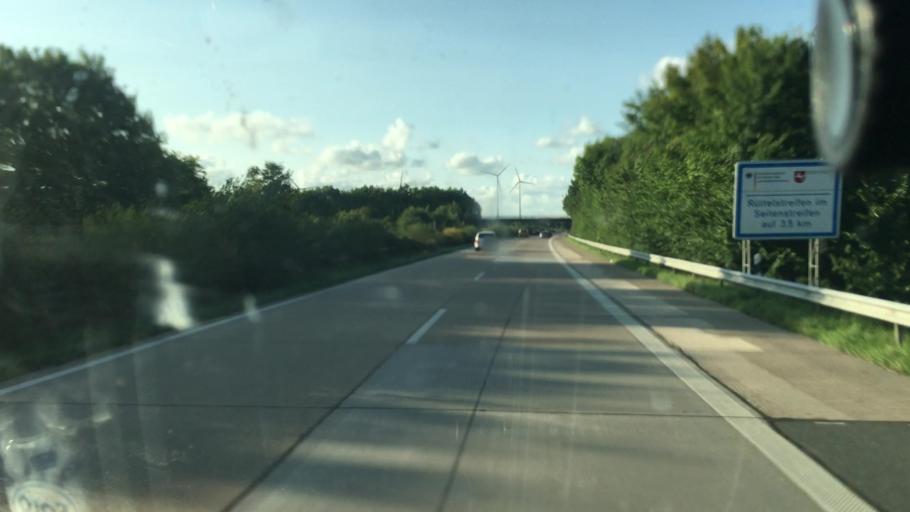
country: DE
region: Lower Saxony
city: Sande
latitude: 53.4884
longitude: 8.0031
